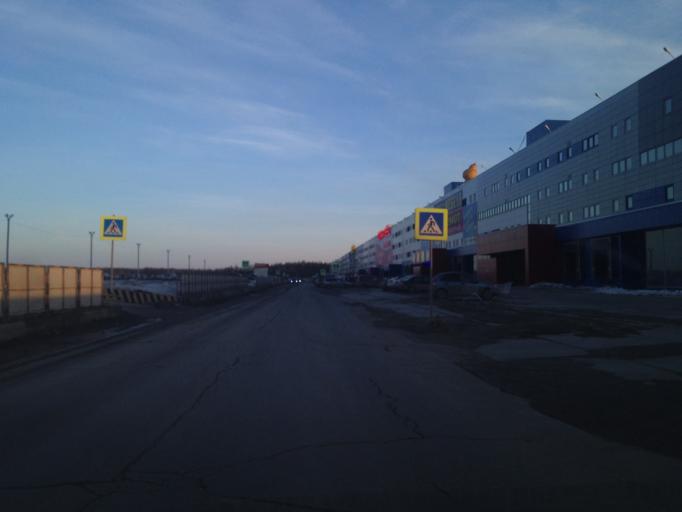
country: RU
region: Sverdlovsk
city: Istok
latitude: 56.7625
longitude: 60.7488
